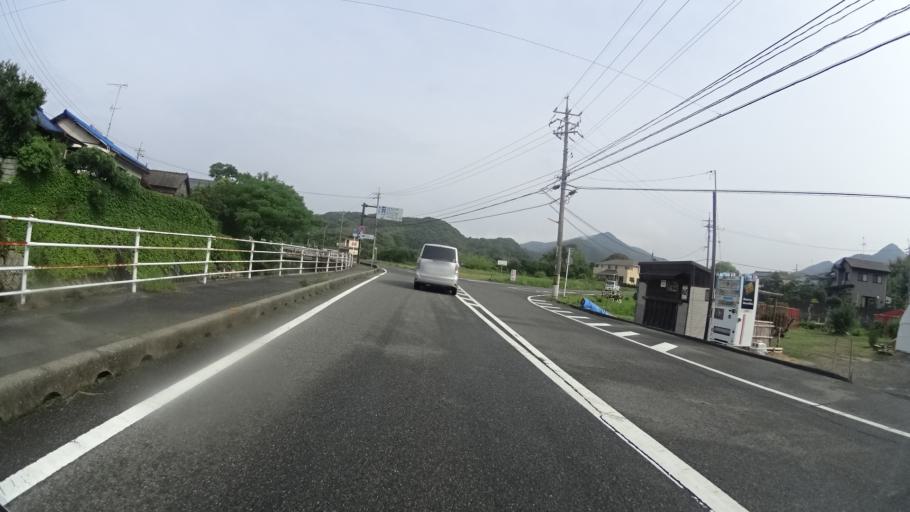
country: JP
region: Yamaguchi
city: Shimonoseki
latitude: 34.0886
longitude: 130.8819
